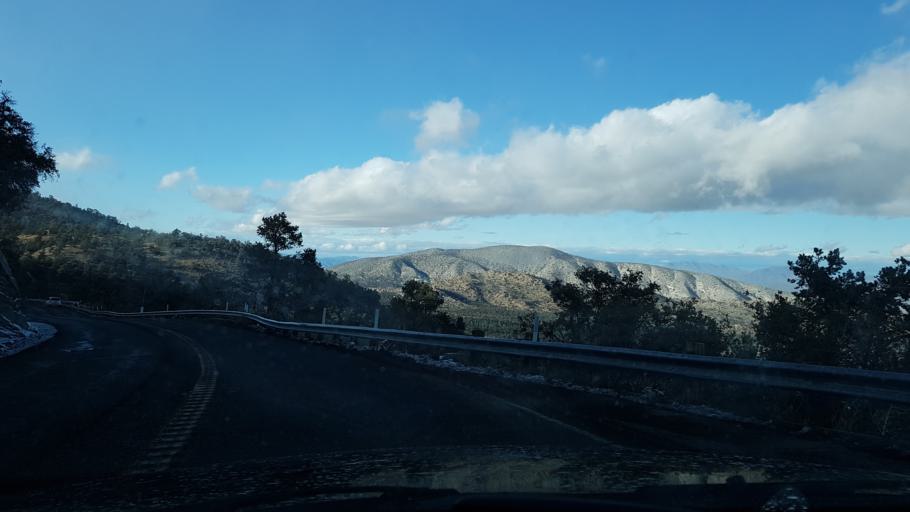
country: US
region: California
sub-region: San Bernardino County
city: Big Bear City
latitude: 34.2955
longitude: -116.7983
